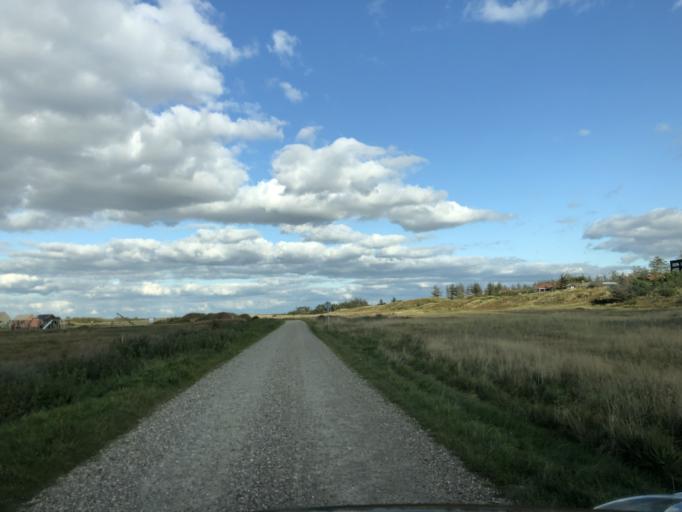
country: DK
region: Central Jutland
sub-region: Holstebro Kommune
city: Ulfborg
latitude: 56.3290
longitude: 8.1466
